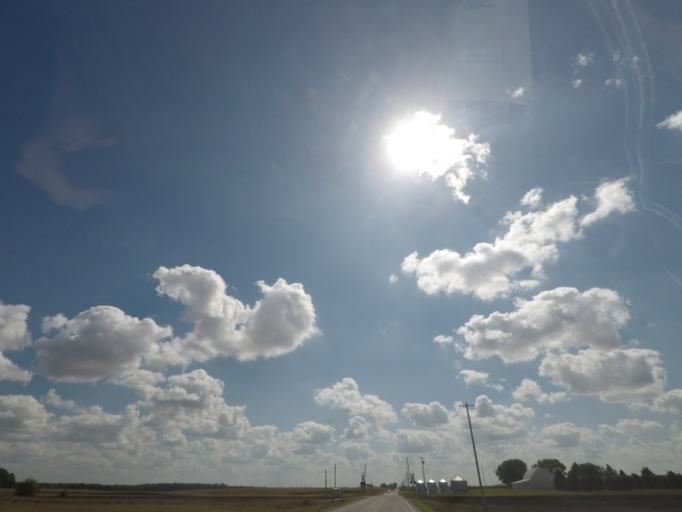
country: US
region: Iowa
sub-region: Story County
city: Nevada
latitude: 42.0254
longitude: -93.4058
